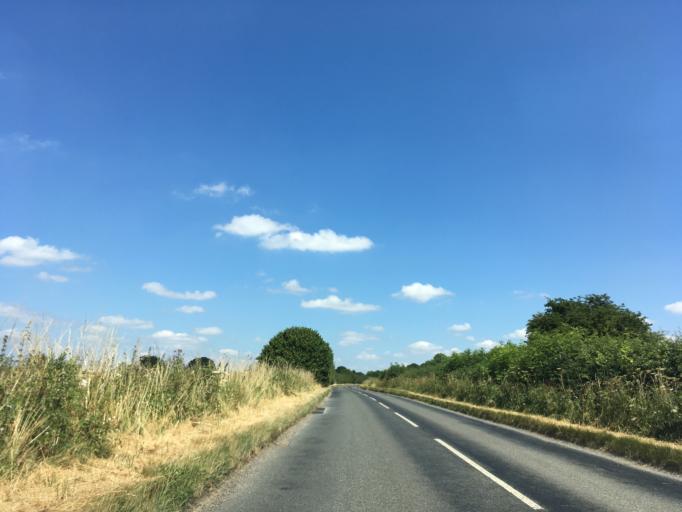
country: GB
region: England
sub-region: Gloucestershire
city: Stroud
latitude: 51.7502
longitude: -2.1797
